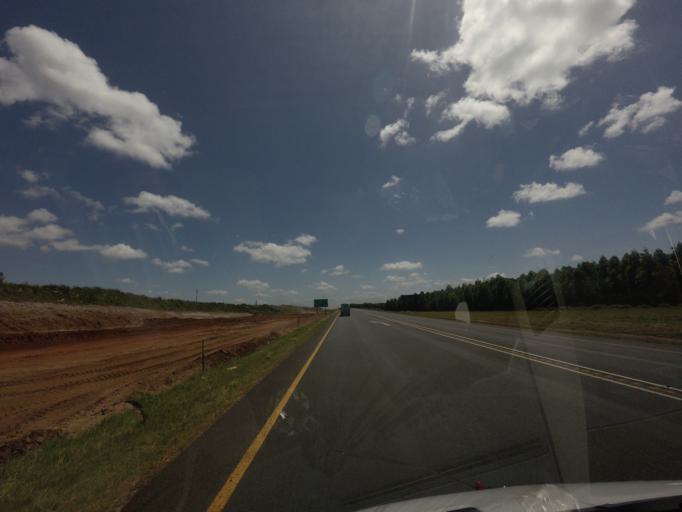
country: ZA
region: KwaZulu-Natal
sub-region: uThungulu District Municipality
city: Empangeni
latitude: -28.8036
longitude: 31.9185
